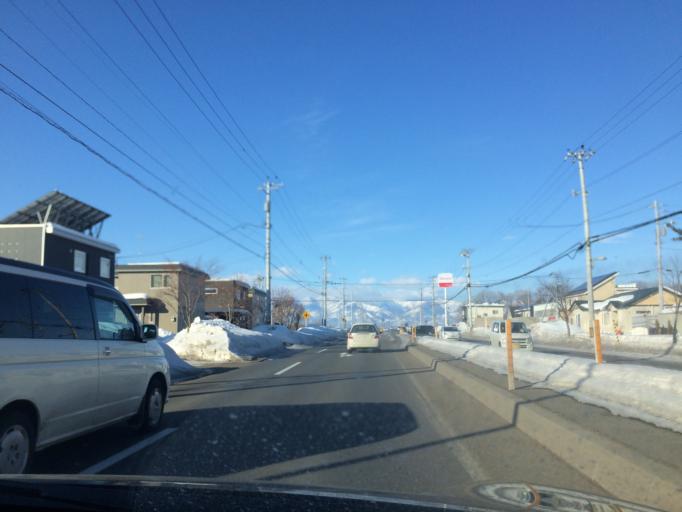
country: JP
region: Hokkaido
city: Obihiro
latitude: 42.9125
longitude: 143.0715
